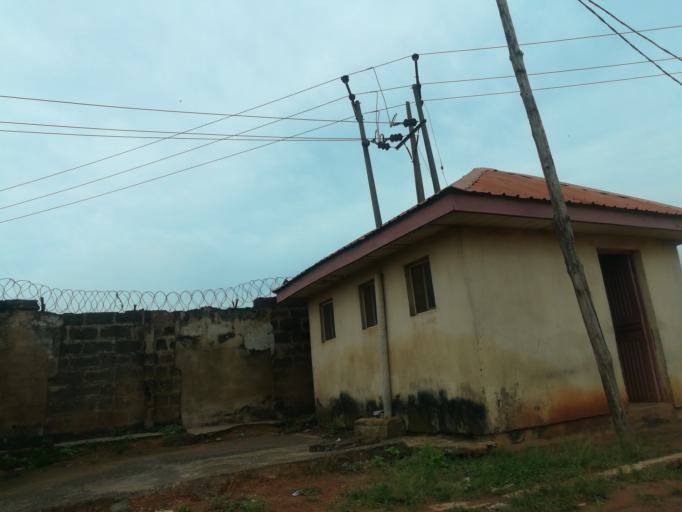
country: NG
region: Oyo
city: Ibadan
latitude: 7.3641
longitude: 3.9278
